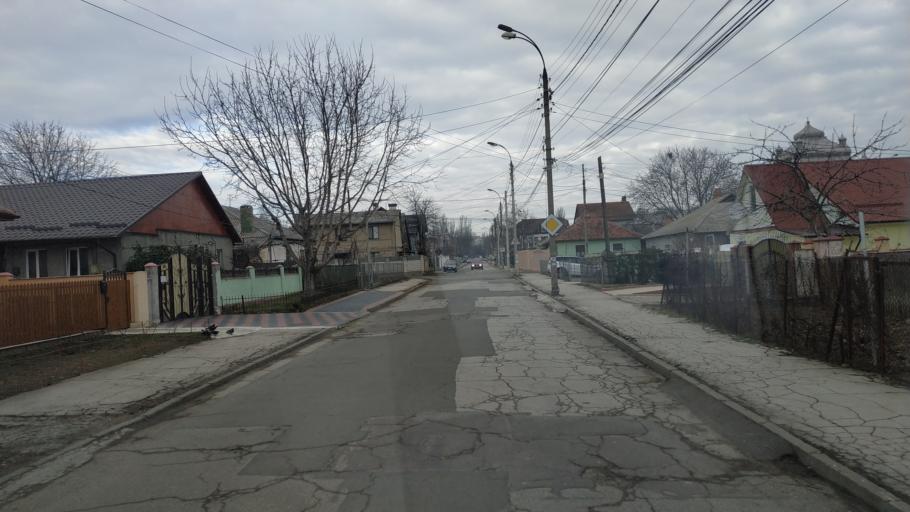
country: MD
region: Chisinau
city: Vatra
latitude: 47.0333
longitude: 28.7856
